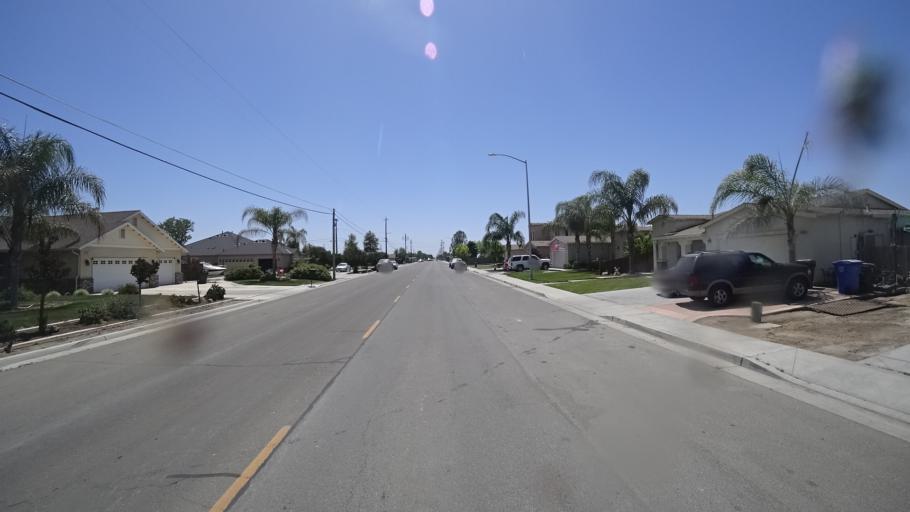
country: US
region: California
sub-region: Kings County
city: Corcoran
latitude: 36.1117
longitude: -119.5721
